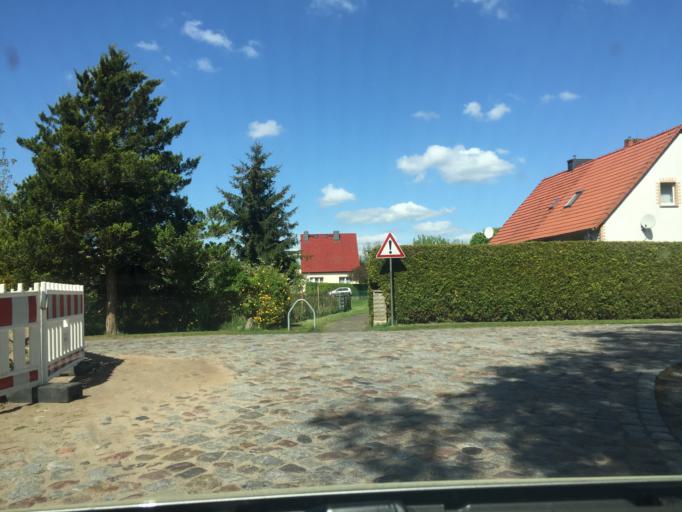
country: DE
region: Mecklenburg-Vorpommern
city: Torgelow
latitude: 53.6369
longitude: 14.0353
